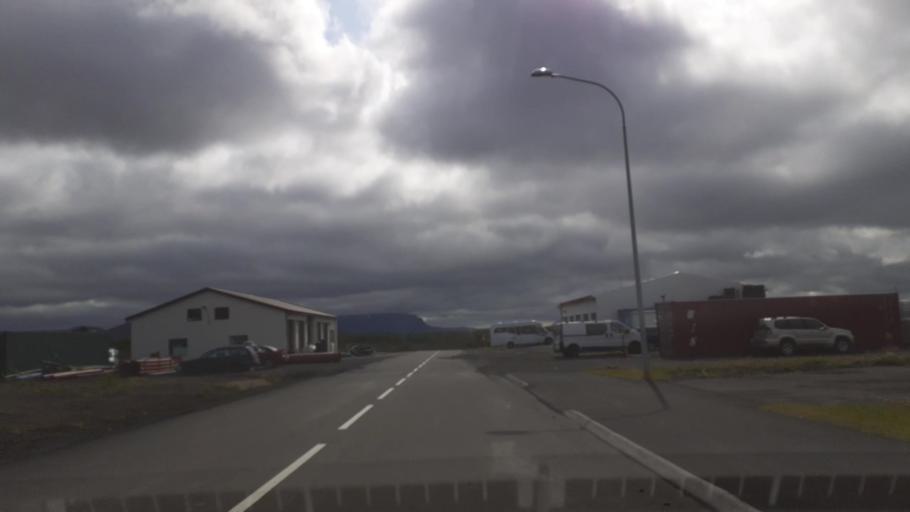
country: IS
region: Northeast
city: Laugar
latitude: 65.6403
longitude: -16.8958
